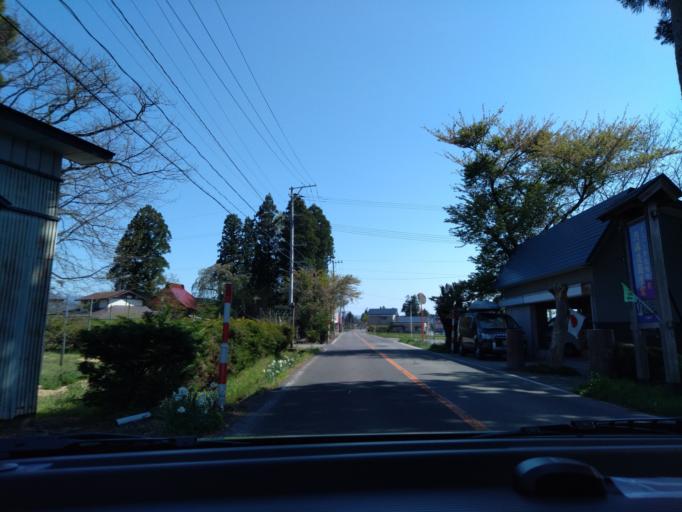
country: JP
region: Akita
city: Kakunodatemachi
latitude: 39.5656
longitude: 140.5833
